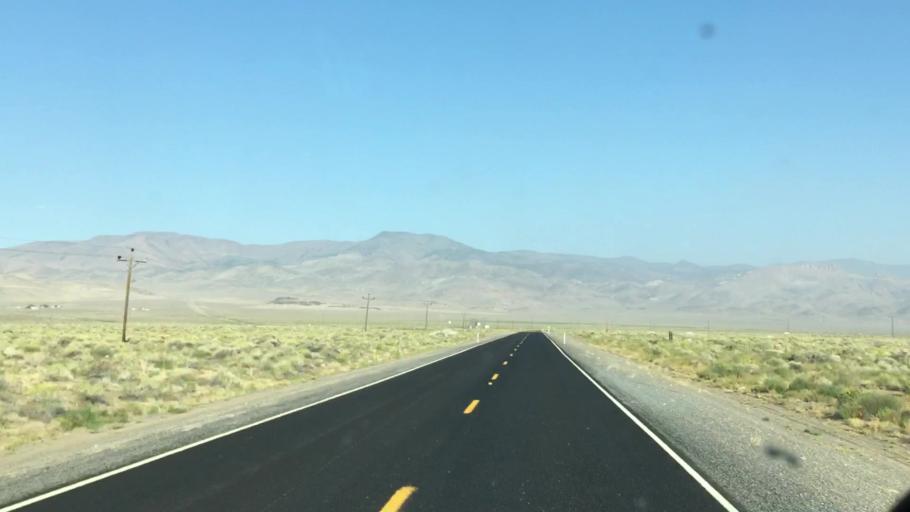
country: US
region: Nevada
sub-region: Lyon County
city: Fernley
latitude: 39.6484
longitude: -119.3186
